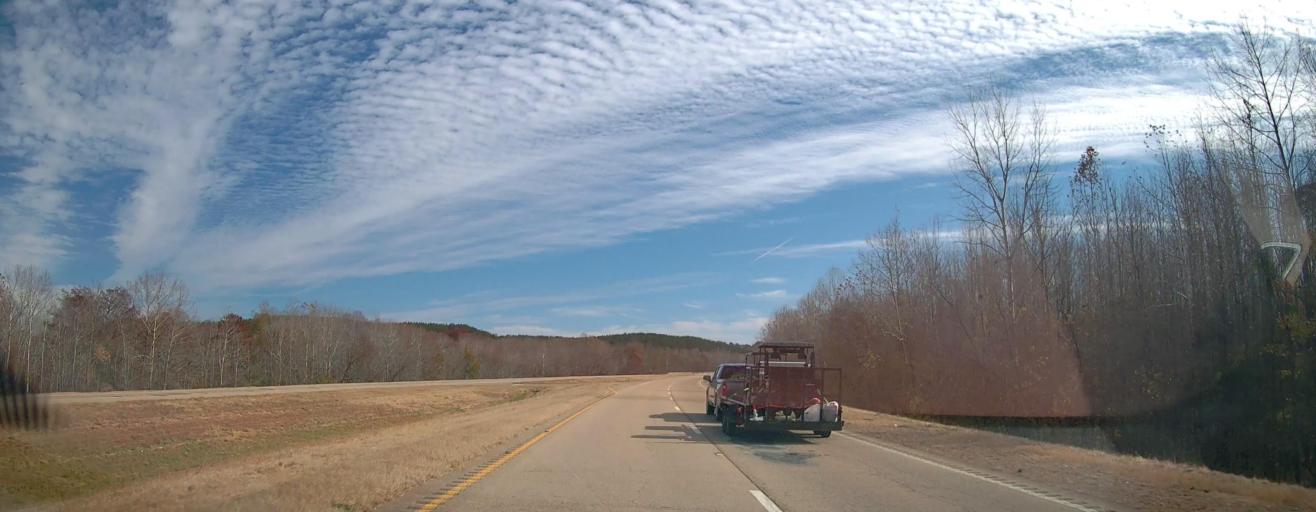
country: US
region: Mississippi
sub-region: Alcorn County
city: Corinth
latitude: 34.9455
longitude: -88.7900
